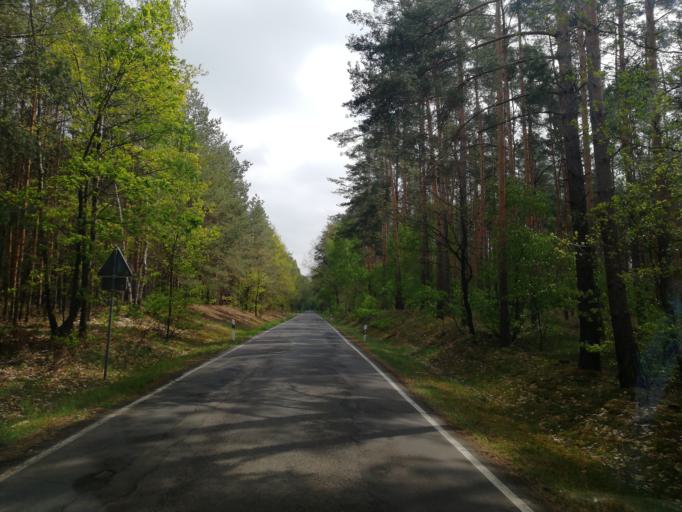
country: DE
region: Brandenburg
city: Herzberg
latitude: 51.6453
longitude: 13.1593
